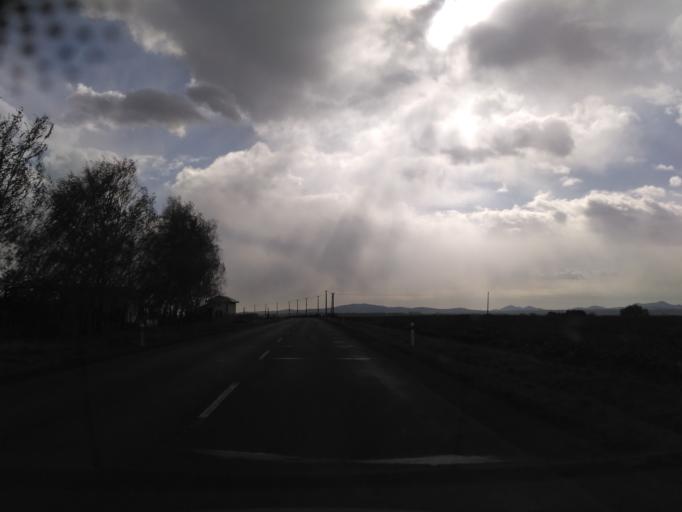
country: SK
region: Kosicky
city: Secovce
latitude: 48.6633
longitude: 21.6631
